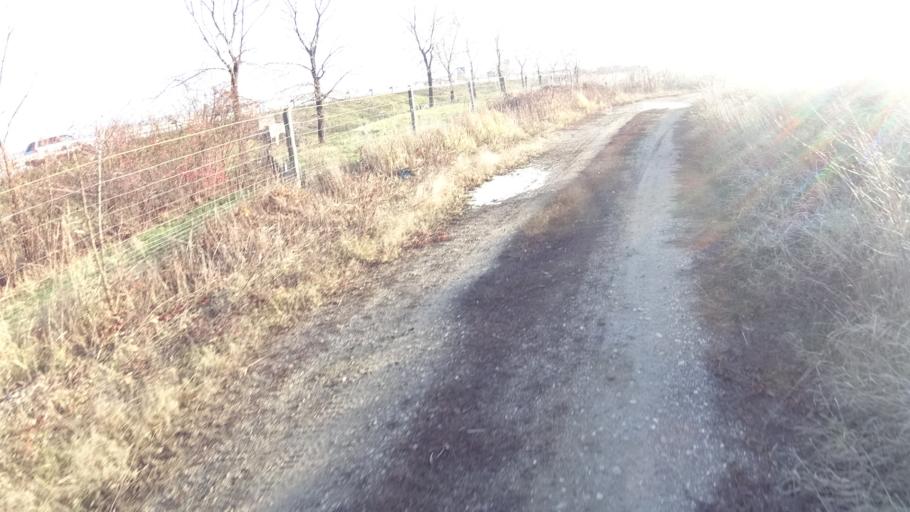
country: HU
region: Borsod-Abauj-Zemplen
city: Onod
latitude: 47.9843
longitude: 20.8966
